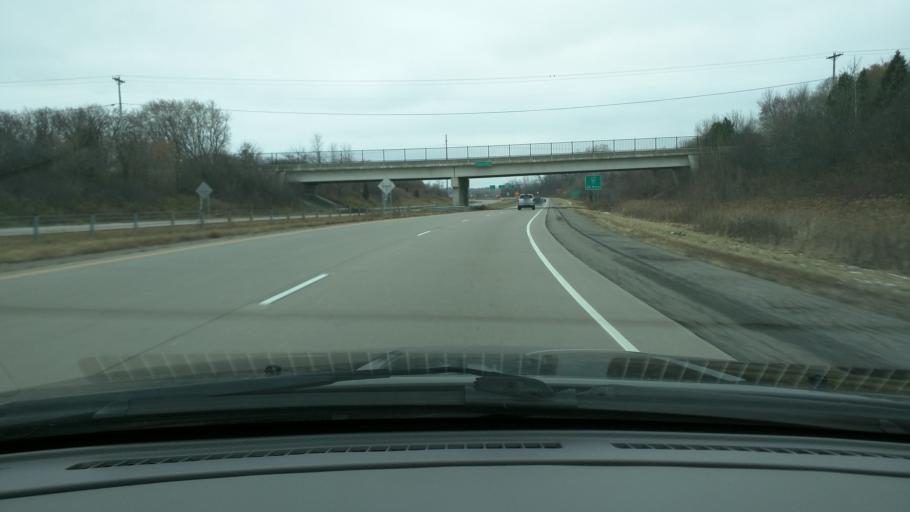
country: US
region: Minnesota
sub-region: Dakota County
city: Mendota Heights
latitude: 44.8793
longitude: -93.1634
